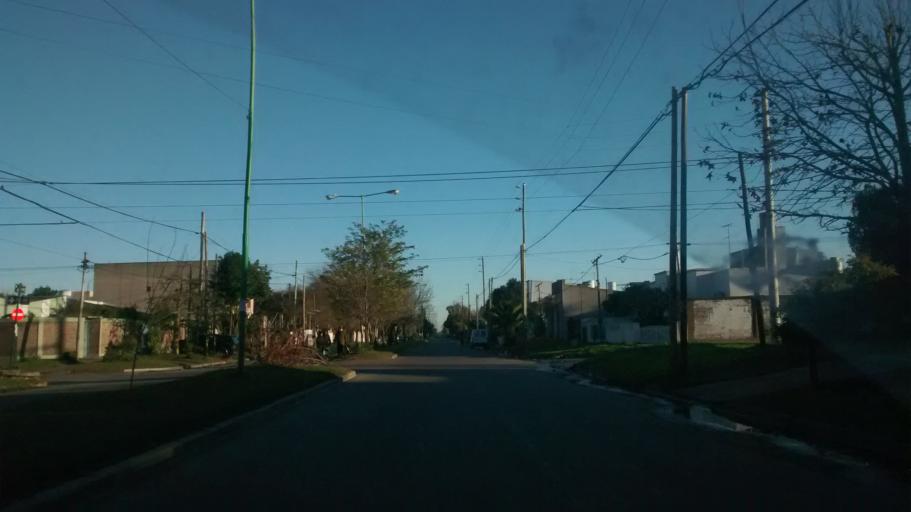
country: AR
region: Buenos Aires
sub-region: Partido de La Plata
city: La Plata
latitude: -34.9579
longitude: -57.9750
